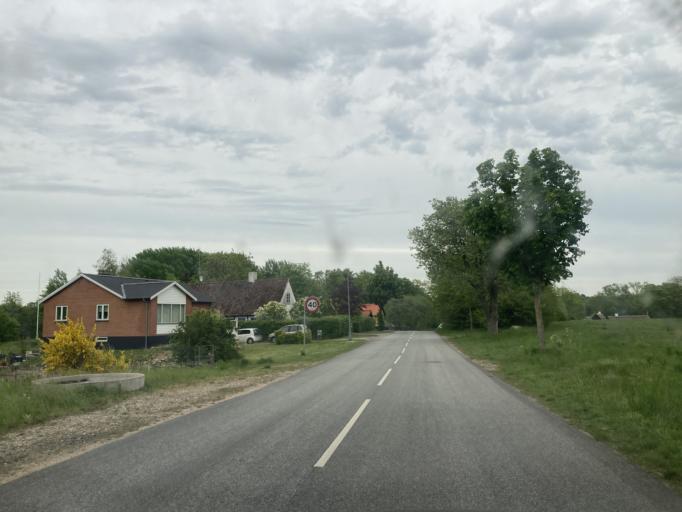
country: DK
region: Zealand
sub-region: Roskilde Kommune
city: Svogerslev
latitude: 55.6345
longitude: 11.9836
